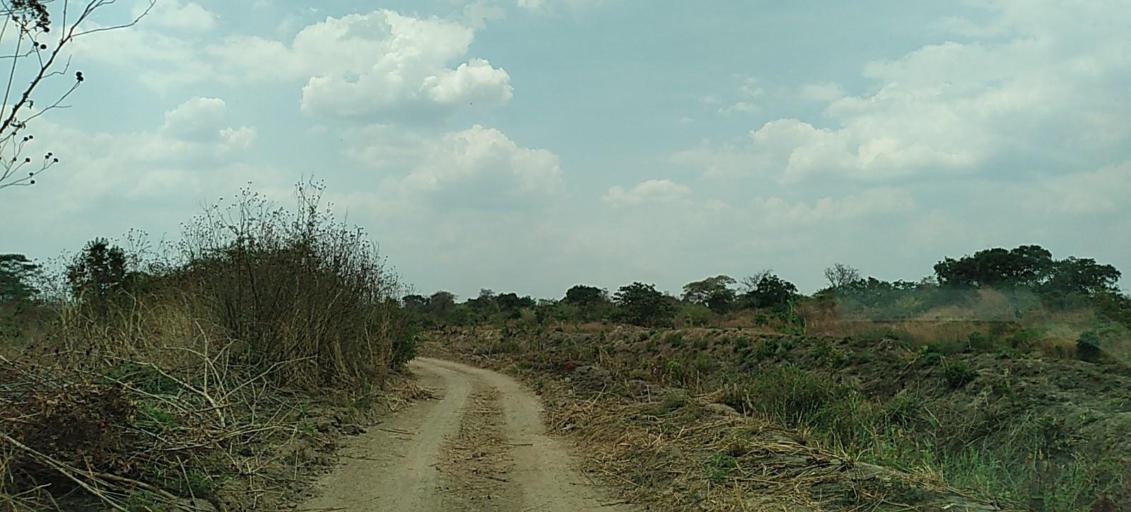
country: ZM
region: Copperbelt
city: Chililabombwe
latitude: -12.3539
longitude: 27.8029
